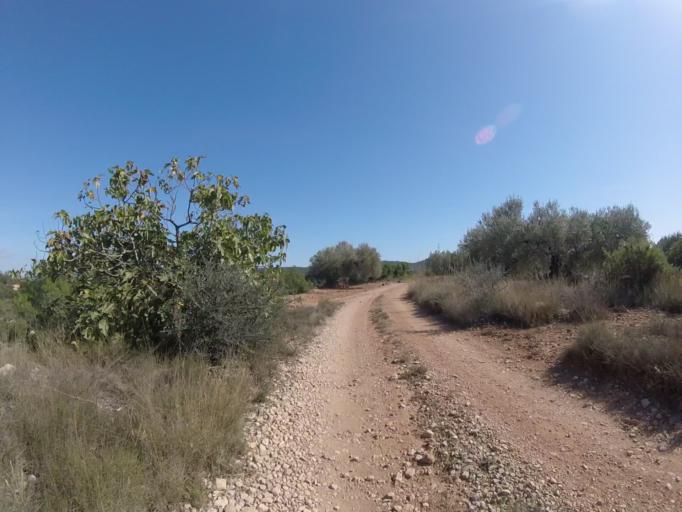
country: ES
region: Valencia
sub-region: Provincia de Castello
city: Cuevas de Vinroma
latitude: 40.2803
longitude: 0.0857
